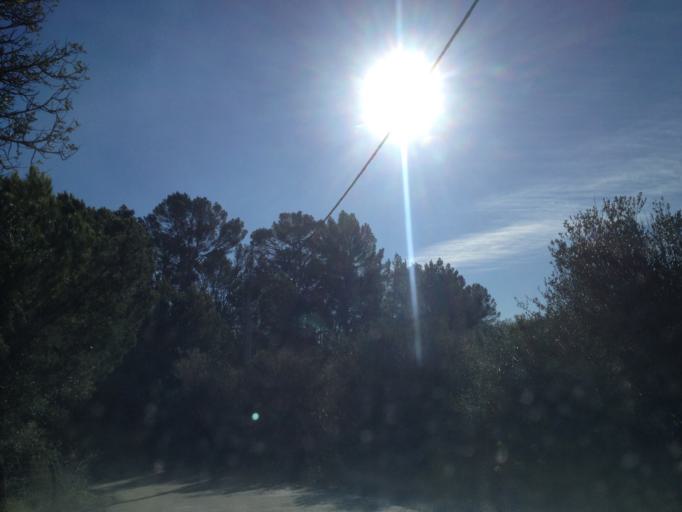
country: ES
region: Balearic Islands
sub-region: Illes Balears
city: Sineu
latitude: 39.6528
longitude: 3.0361
